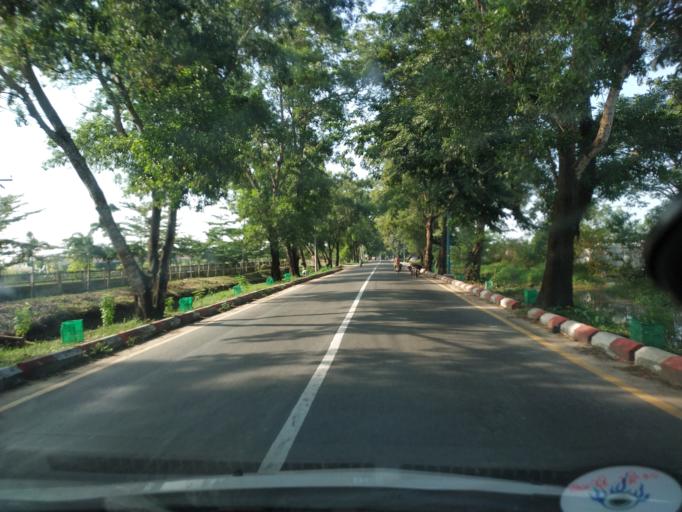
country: MM
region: Ayeyarwady
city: Pathein
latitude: 16.8055
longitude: 94.7580
